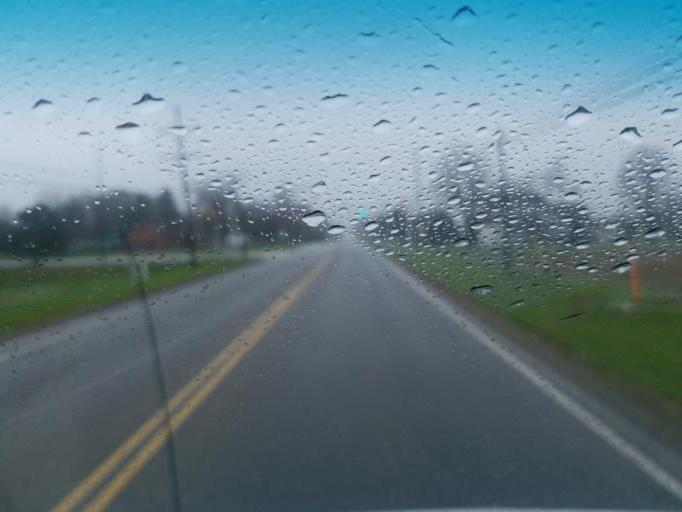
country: US
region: Ohio
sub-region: Hancock County
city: Findlay
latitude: 41.0954
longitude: -83.6499
